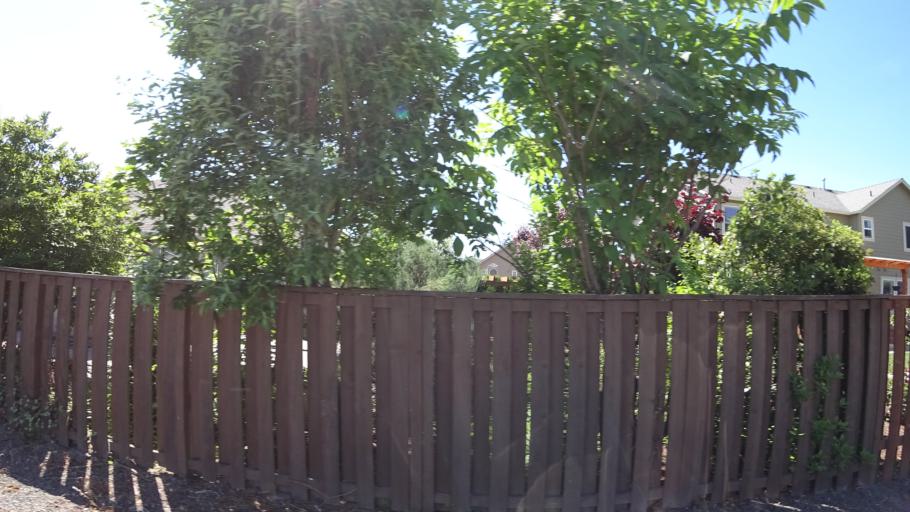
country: US
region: Oregon
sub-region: Clackamas County
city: Happy Valley
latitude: 45.4782
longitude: -122.4853
